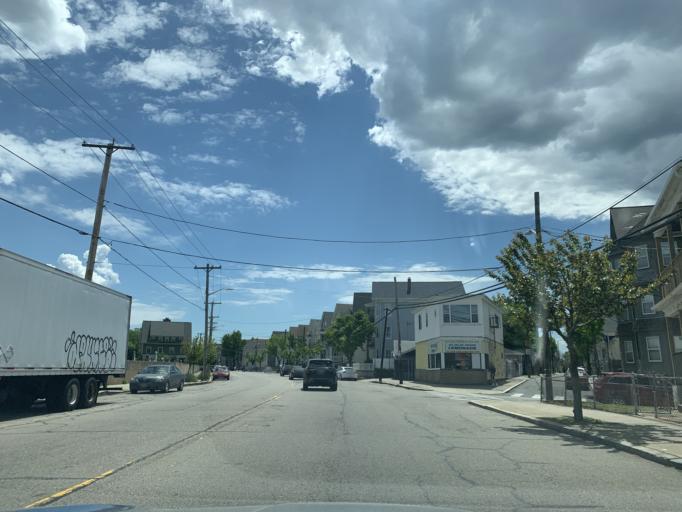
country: US
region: Rhode Island
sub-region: Providence County
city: Providence
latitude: 41.8388
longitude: -71.4254
